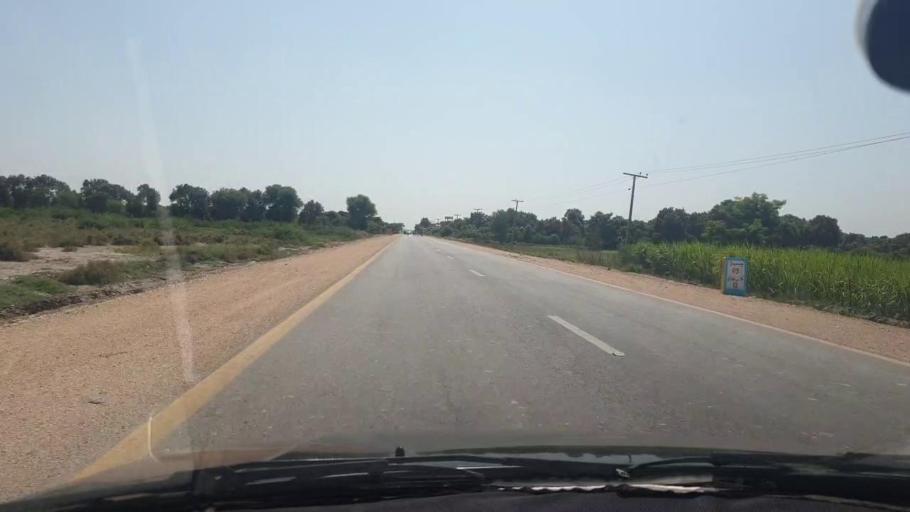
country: PK
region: Sindh
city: Chambar
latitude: 25.3249
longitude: 68.8006
